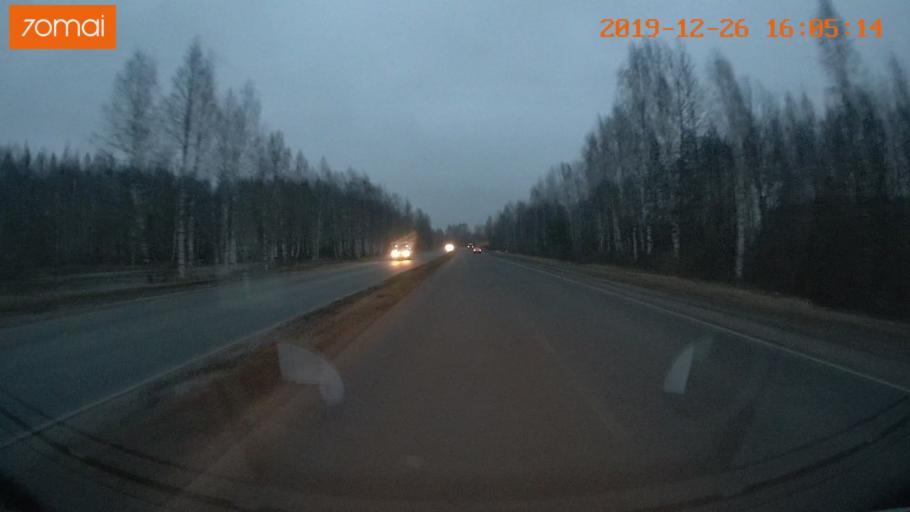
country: RU
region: Jaroslavl
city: Rybinsk
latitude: 58.0065
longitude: 38.8905
